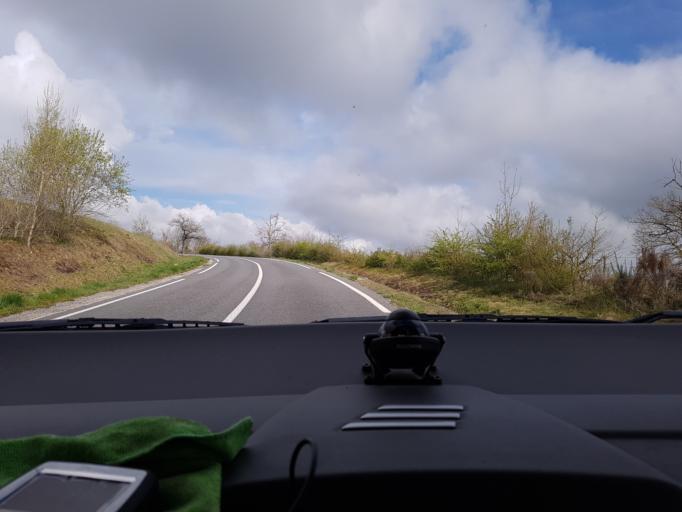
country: FR
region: Midi-Pyrenees
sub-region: Departement de l'Aveyron
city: Moyrazes
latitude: 44.3779
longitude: 2.4580
